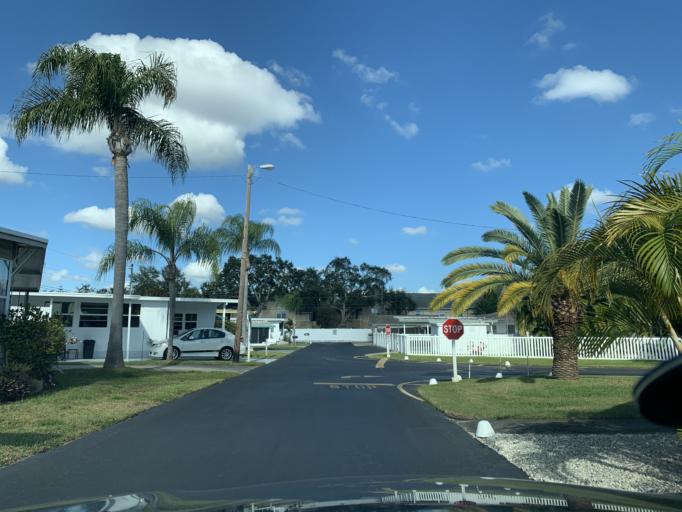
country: US
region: Florida
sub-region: Pinellas County
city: Kenneth City
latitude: 27.8093
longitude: -82.7375
